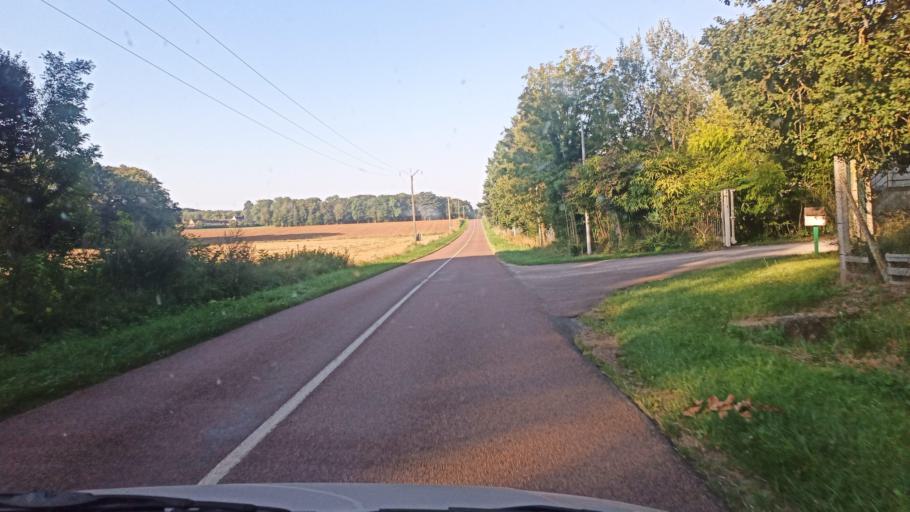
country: FR
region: Bourgogne
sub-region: Departement de l'Yonne
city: Pont-sur-Yonne
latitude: 48.2543
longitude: 3.1687
